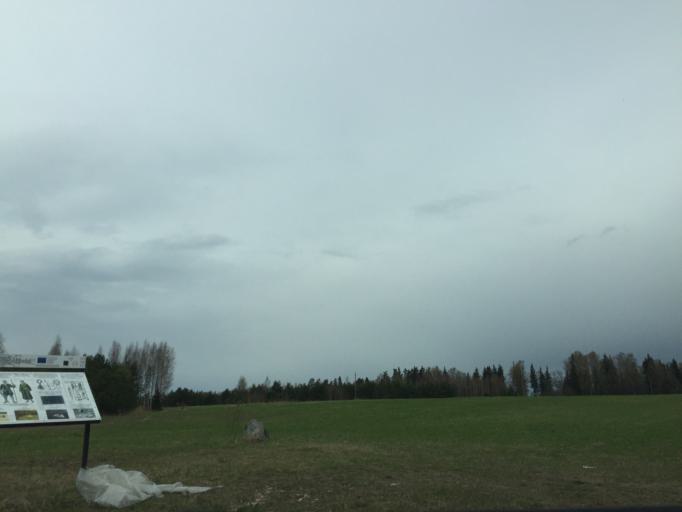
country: LV
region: Priekuli
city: Priekuli
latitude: 57.3006
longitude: 25.4105
